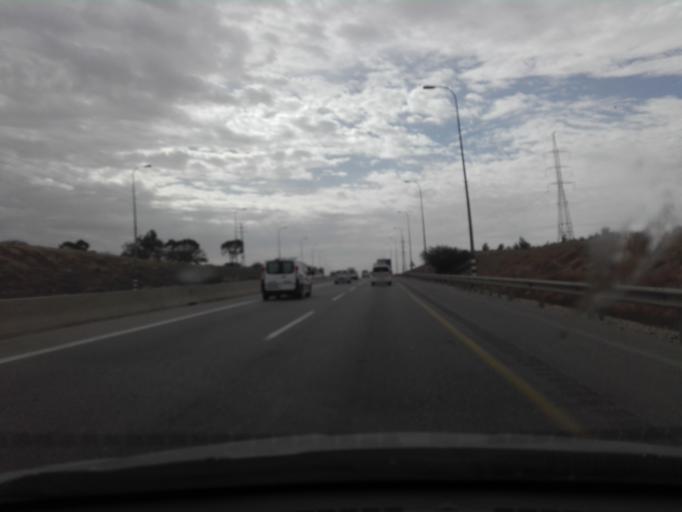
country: IL
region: Southern District
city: Lehavim
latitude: 31.3486
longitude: 34.7914
